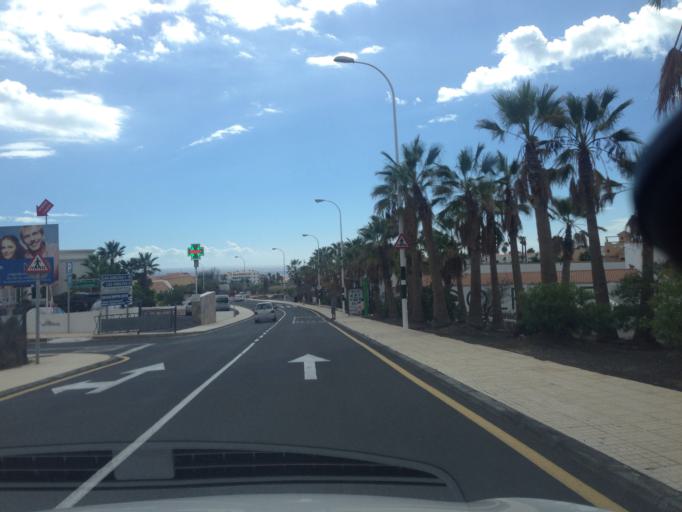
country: ES
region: Canary Islands
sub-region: Provincia de Santa Cruz de Tenerife
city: Las Rosas
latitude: 28.0333
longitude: -16.6114
